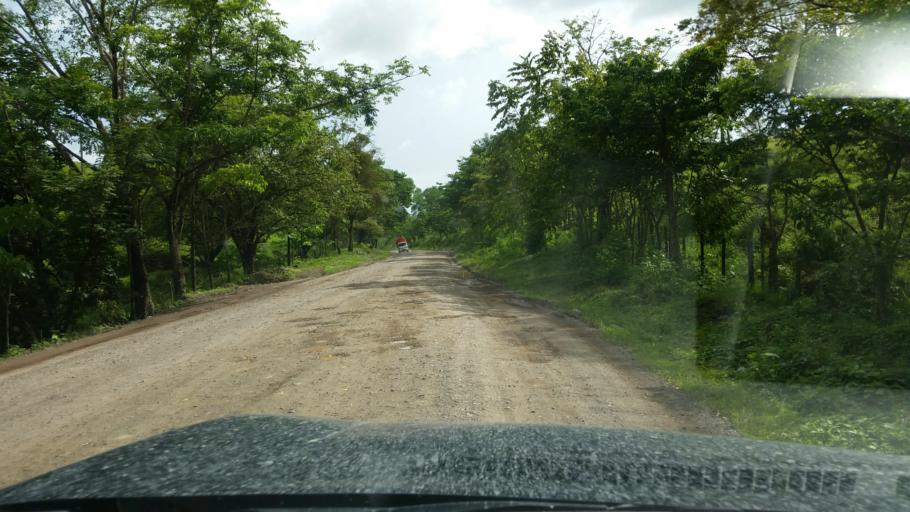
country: NI
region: Atlantico Norte (RAAN)
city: Siuna
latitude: 13.5979
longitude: -84.8030
